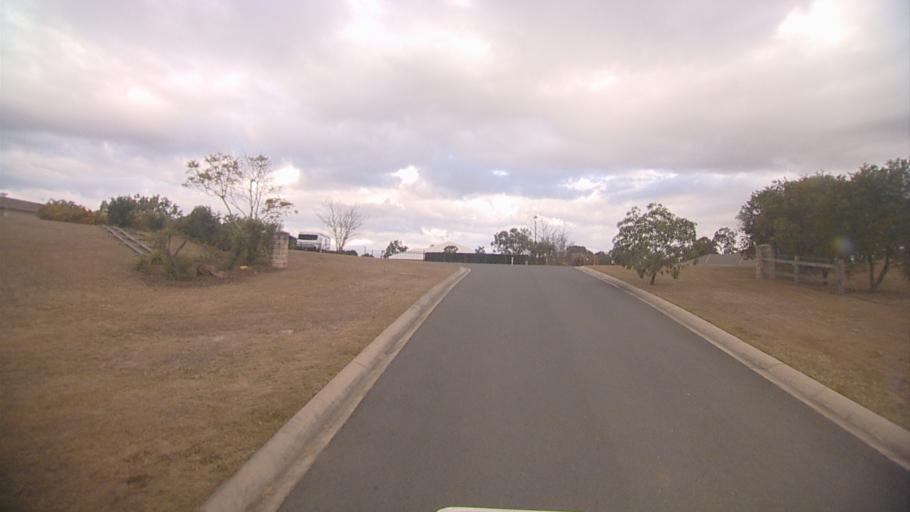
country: AU
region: Queensland
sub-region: Logan
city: Cedar Vale
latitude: -27.8661
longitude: 153.0819
